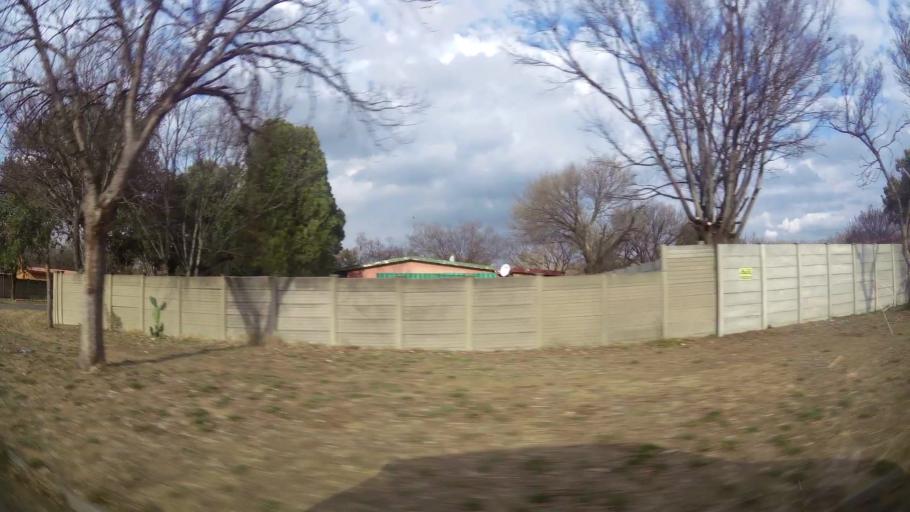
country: ZA
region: Orange Free State
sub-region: Fezile Dabi District Municipality
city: Sasolburg
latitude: -26.8058
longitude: 27.8120
